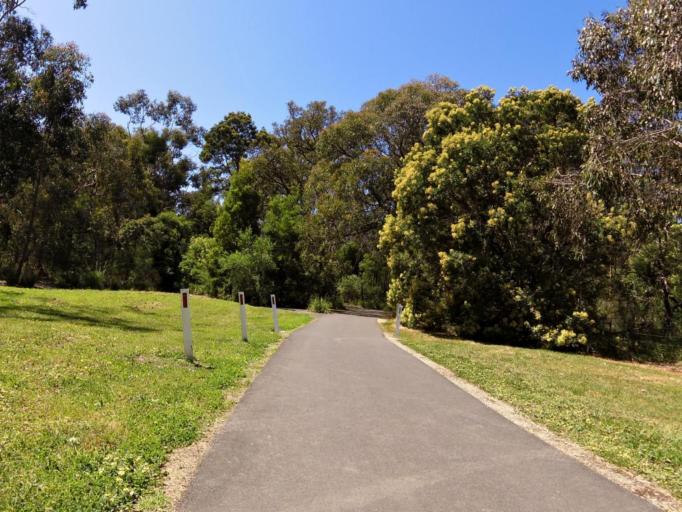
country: AU
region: Victoria
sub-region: Knox
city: Boronia
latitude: -37.8682
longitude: 145.2736
